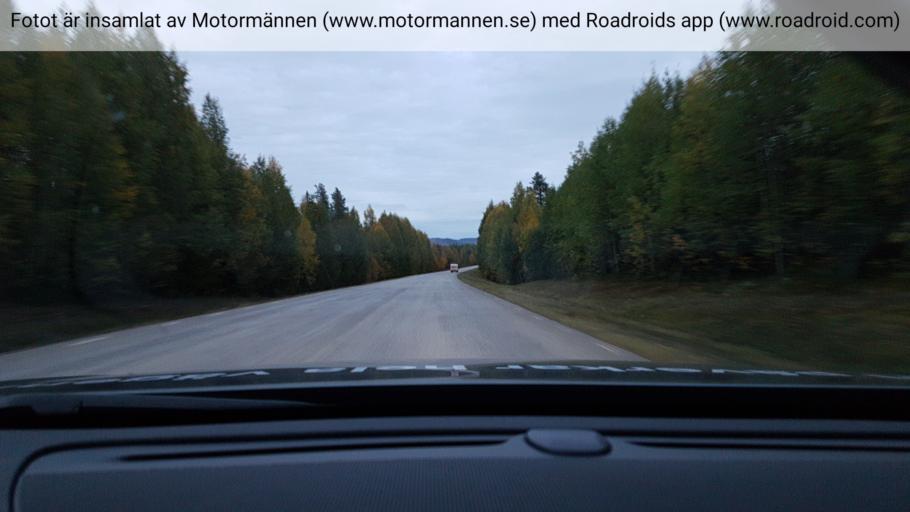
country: SE
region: Norrbotten
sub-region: Alvsbyns Kommun
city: AElvsbyn
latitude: 65.8442
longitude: 20.4894
